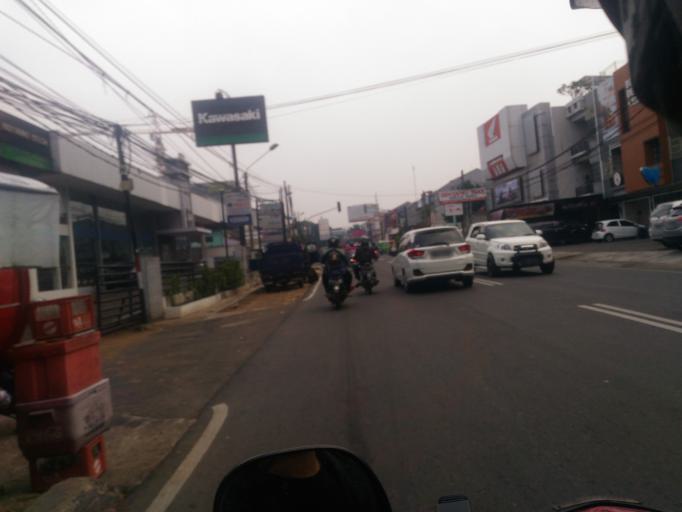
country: ID
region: West Java
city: Bogor
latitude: -6.6320
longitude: 106.8250
